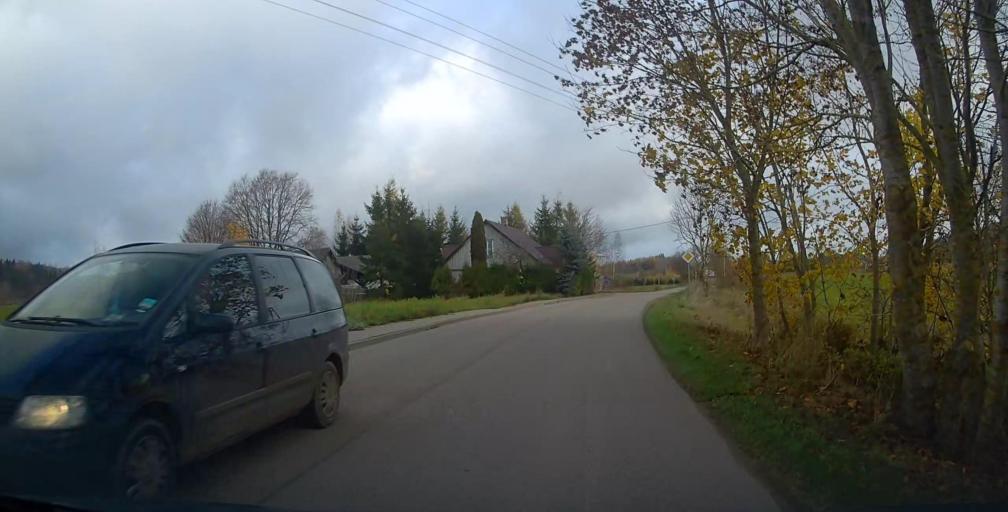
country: PL
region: Podlasie
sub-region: Suwalki
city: Suwalki
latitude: 54.2910
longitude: 22.8790
